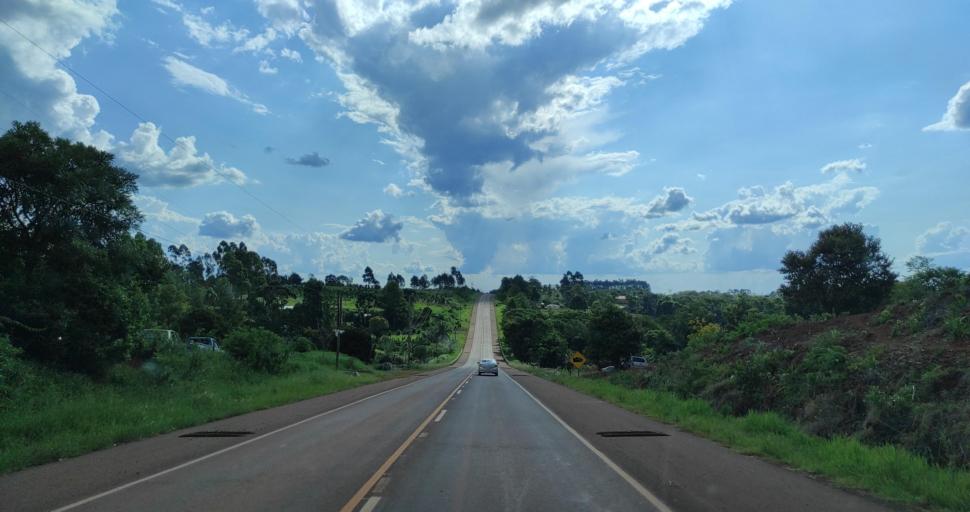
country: AR
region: Misiones
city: Bernardo de Irigoyen
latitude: -26.2938
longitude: -53.7742
